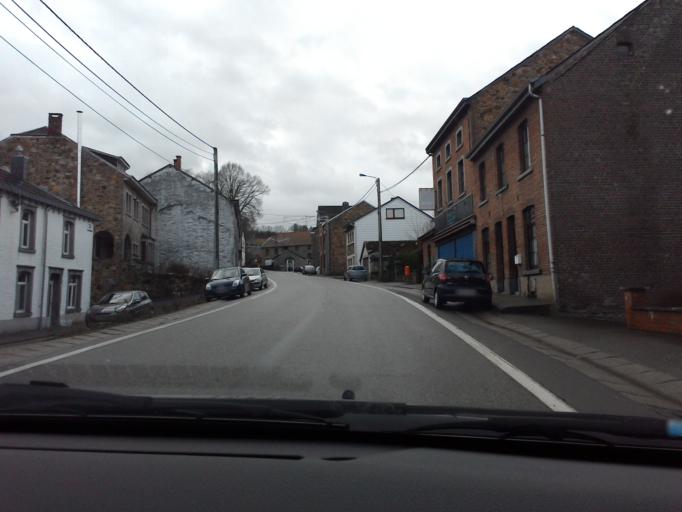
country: BE
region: Wallonia
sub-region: Province du Luxembourg
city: Vielsalm
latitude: 50.3250
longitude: 5.9083
